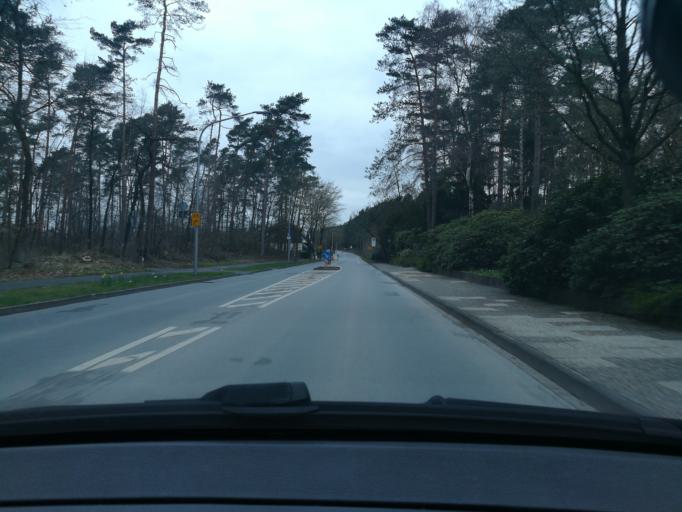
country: DE
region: North Rhine-Westphalia
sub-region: Regierungsbezirk Detmold
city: Oerlinghausen
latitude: 51.9534
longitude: 8.6126
